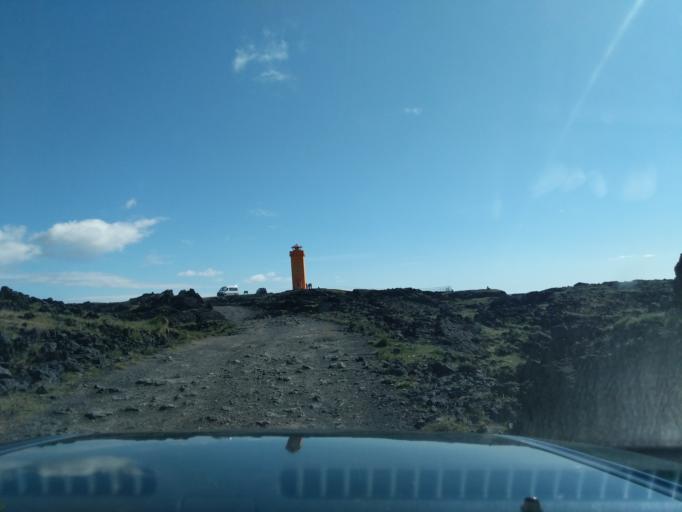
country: IS
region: West
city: Olafsvik
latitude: 64.8651
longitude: -24.0381
